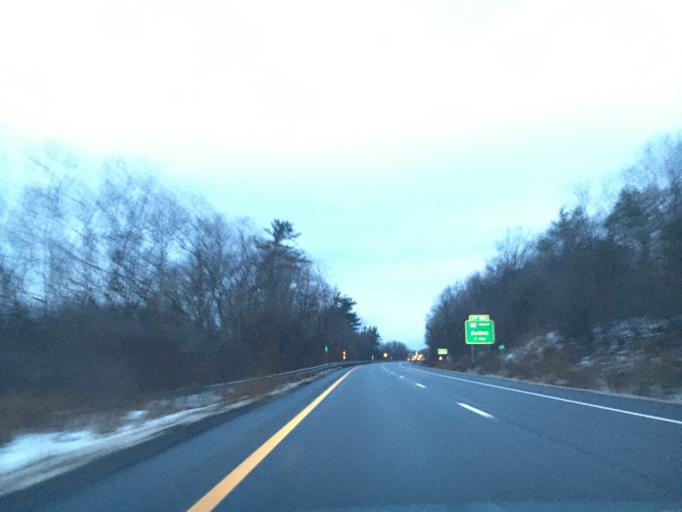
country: US
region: New York
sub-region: Onondaga County
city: Nedrow
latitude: 42.9883
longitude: -76.1335
